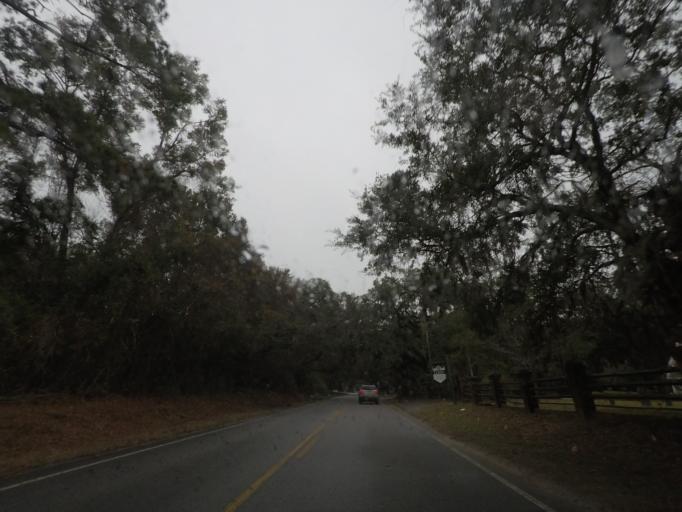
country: US
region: South Carolina
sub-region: Charleston County
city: Seabrook Island
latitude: 32.5698
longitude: -80.2831
